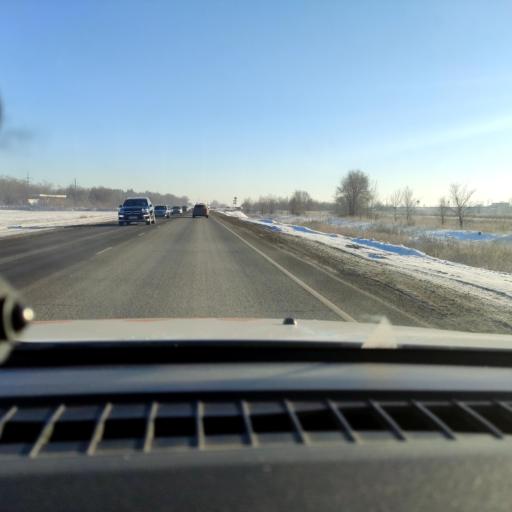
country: RU
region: Samara
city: Samara
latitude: 53.1269
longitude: 50.1656
